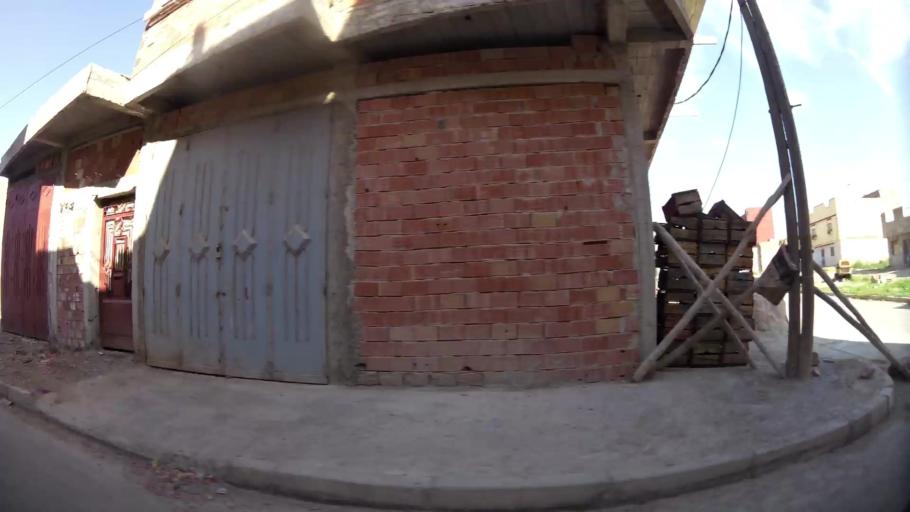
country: MA
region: Oriental
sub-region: Oujda-Angad
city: Oujda
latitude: 34.7185
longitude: -1.8842
